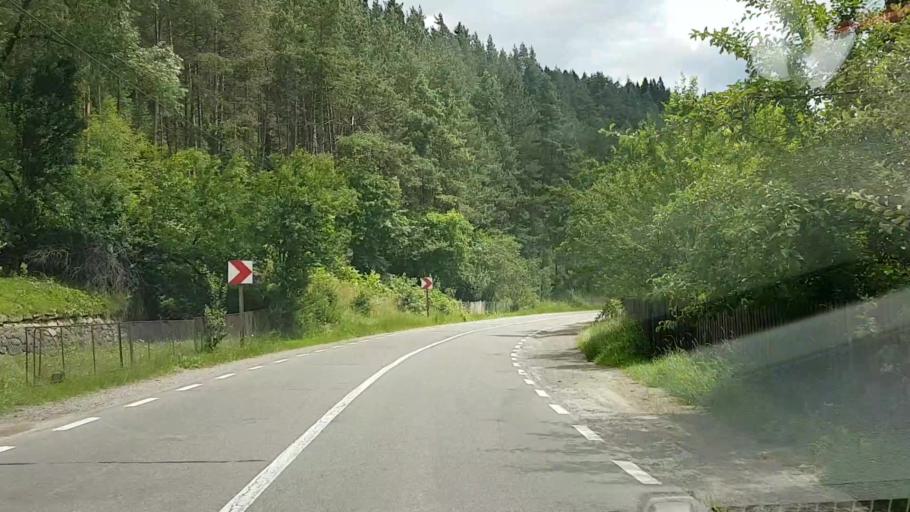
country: RO
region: Neamt
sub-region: Comuna Poiana Teiului
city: Poiana Teiului
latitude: 47.1275
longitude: 25.9054
